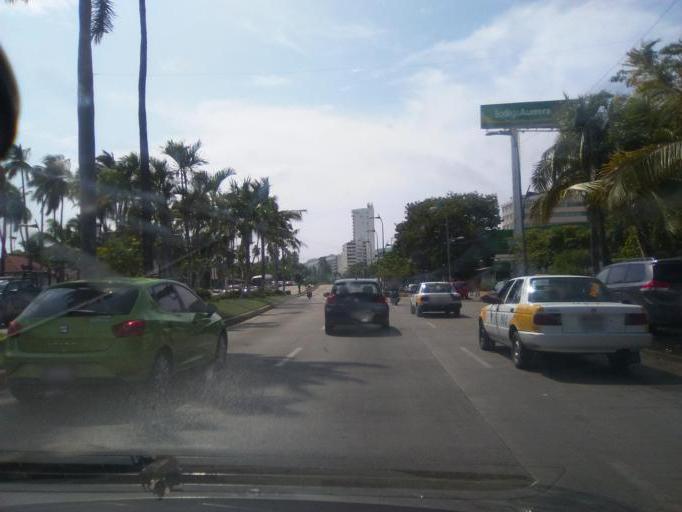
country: MX
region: Guerrero
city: Acapulco de Juarez
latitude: 16.8578
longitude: -99.8910
